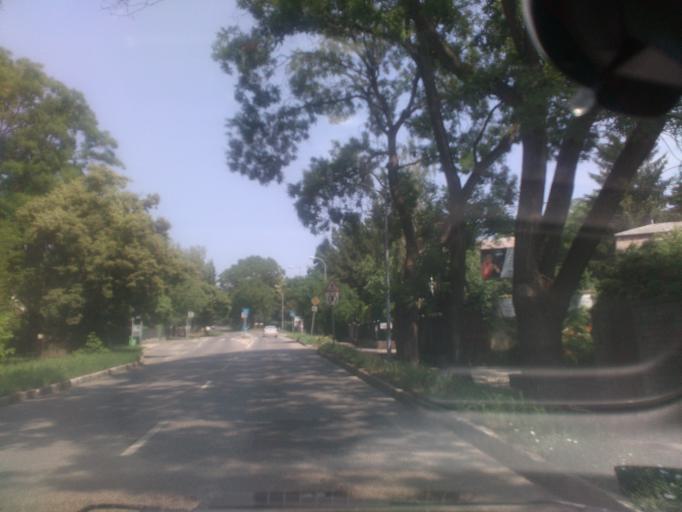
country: HU
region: Pest
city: Budakeszi
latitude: 47.5477
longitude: 18.9647
